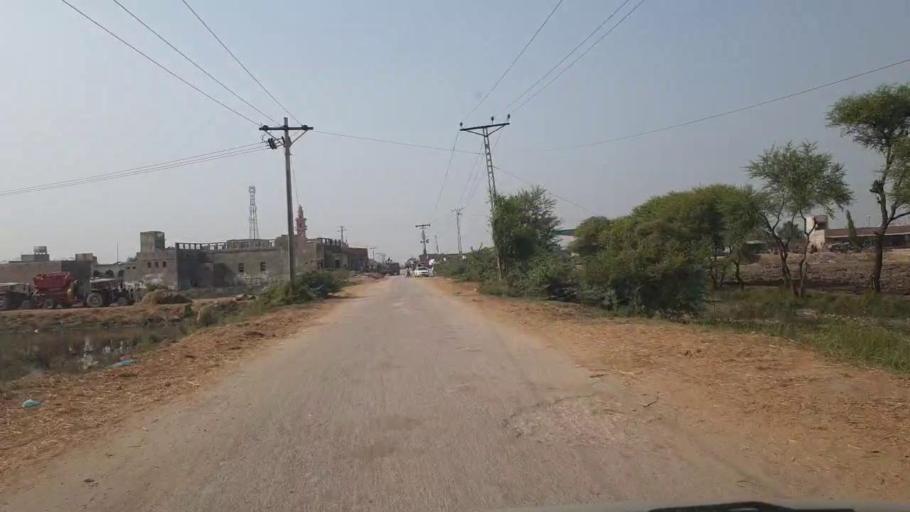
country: PK
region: Sindh
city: Matli
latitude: 25.0337
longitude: 68.6578
